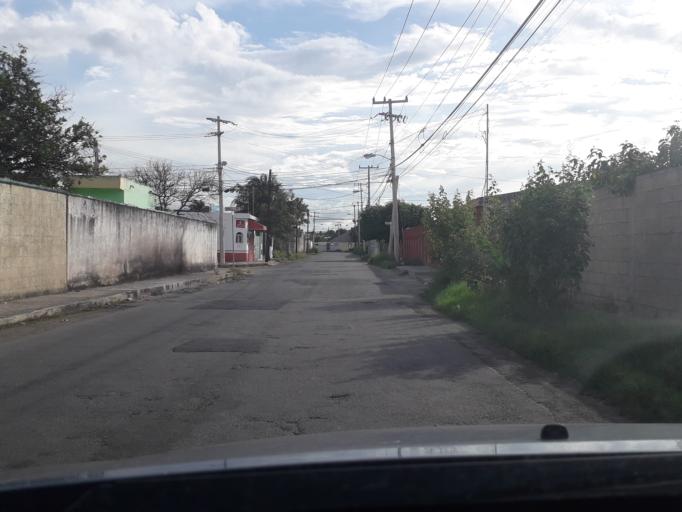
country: MX
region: Yucatan
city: Merida
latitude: 21.0047
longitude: -89.6403
